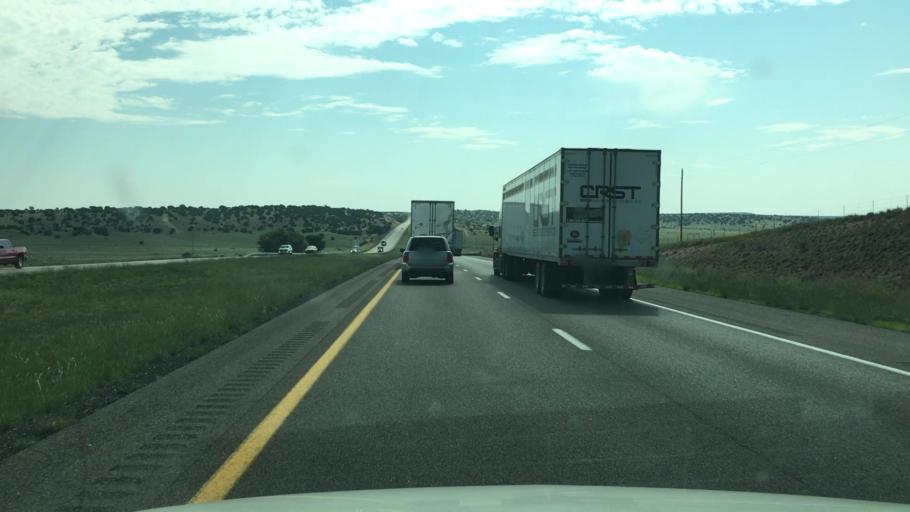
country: US
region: New Mexico
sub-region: Guadalupe County
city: Santa Rosa
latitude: 34.9757
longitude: -104.9779
